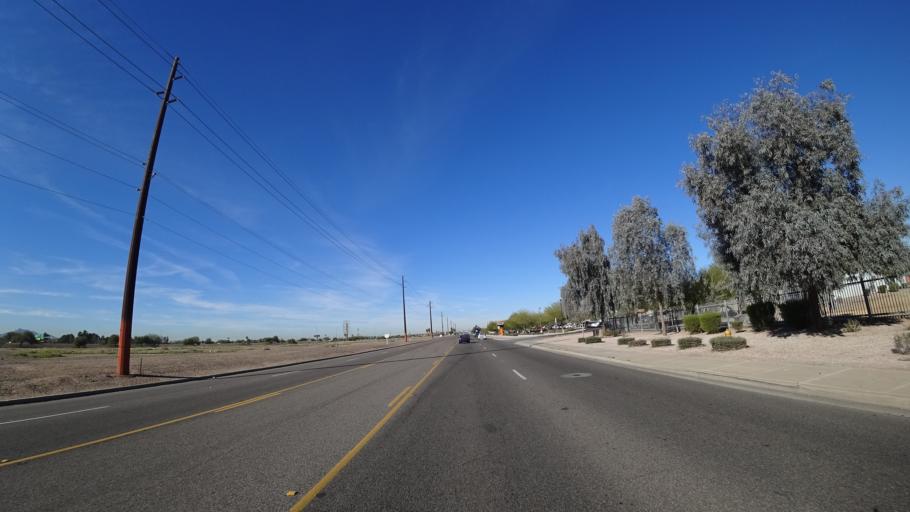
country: US
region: Arizona
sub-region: Maricopa County
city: Tolleson
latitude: 33.4652
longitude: -112.2483
